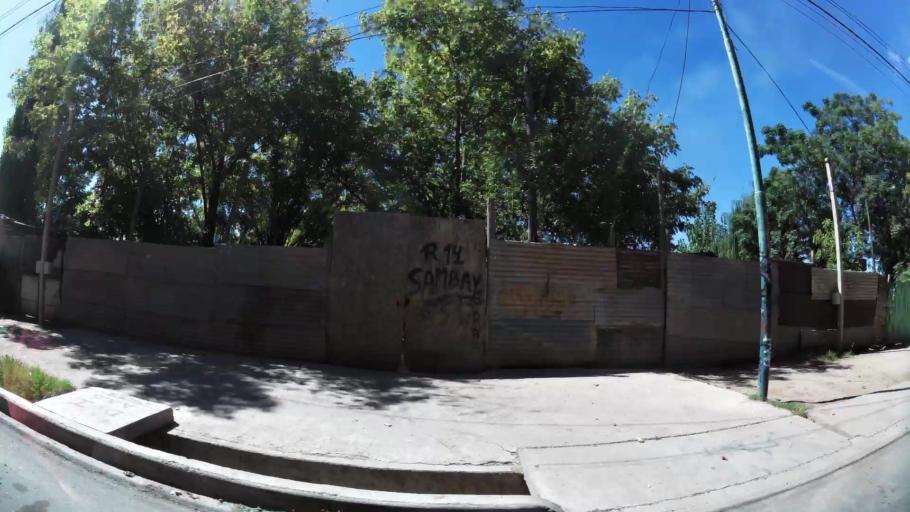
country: AR
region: Mendoza
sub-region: Departamento de Godoy Cruz
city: Godoy Cruz
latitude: -32.9589
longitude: -68.8422
